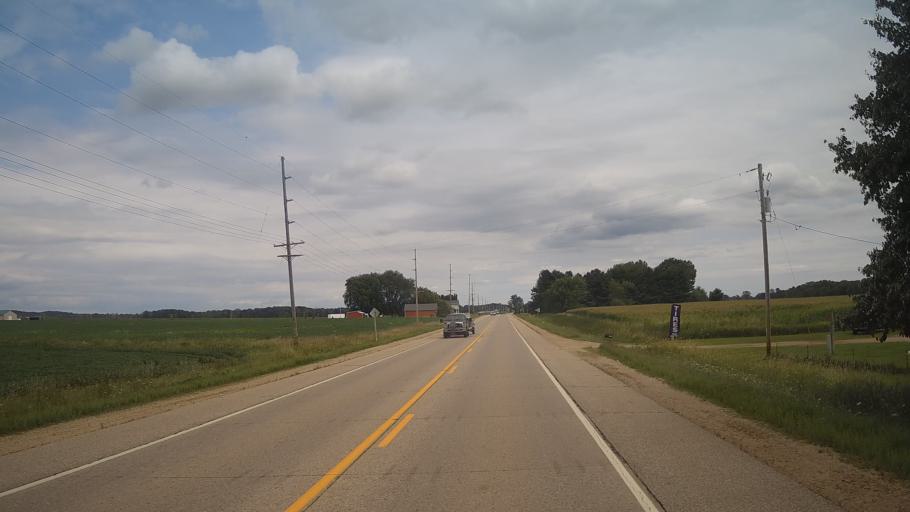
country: US
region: Wisconsin
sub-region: Waushara County
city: Redgranite
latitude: 44.0413
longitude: -89.0375
